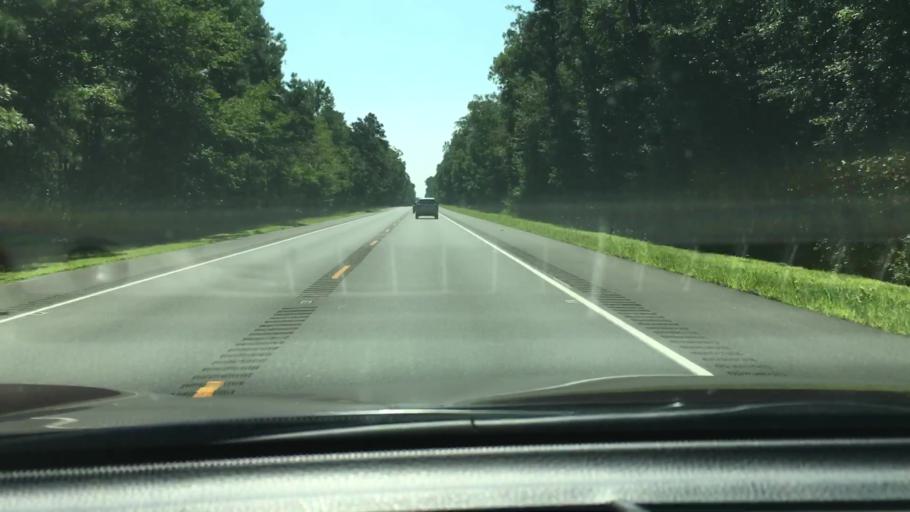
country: US
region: New Jersey
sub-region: Cape May County
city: Woodbine
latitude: 39.3371
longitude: -74.8868
